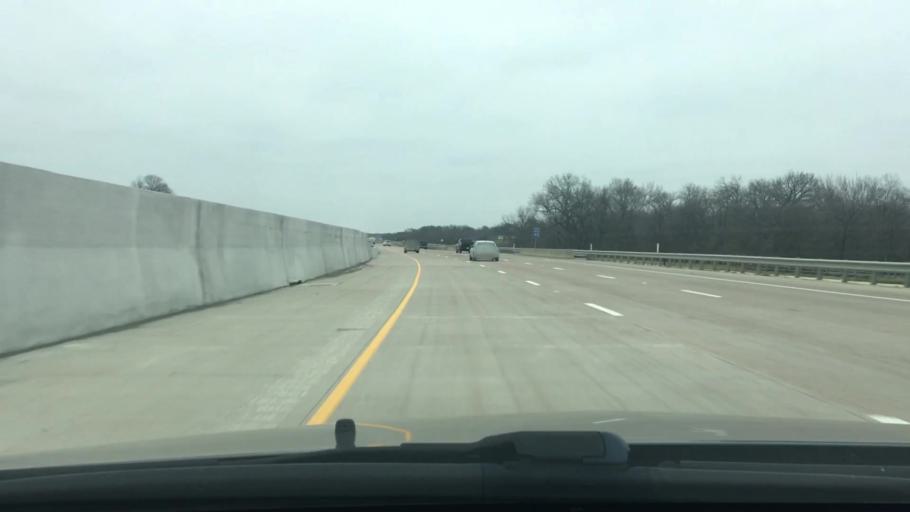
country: US
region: Texas
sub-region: Freestone County
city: Wortham
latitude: 31.9220
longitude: -96.4119
